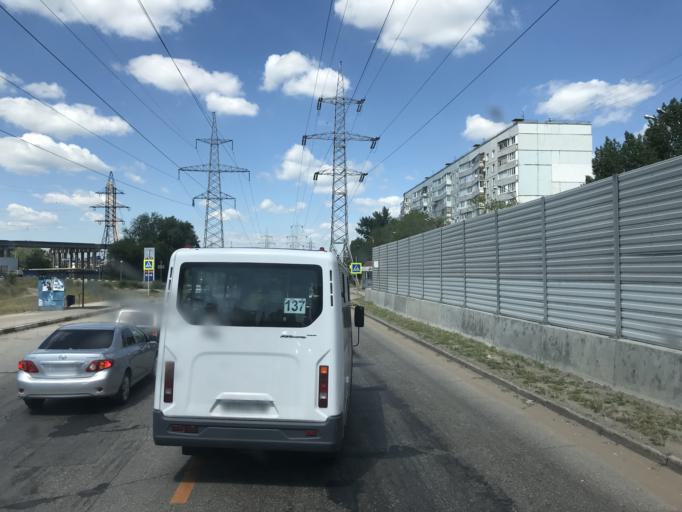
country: RU
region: Samara
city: Zhigulevsk
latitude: 53.4765
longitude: 49.5120
